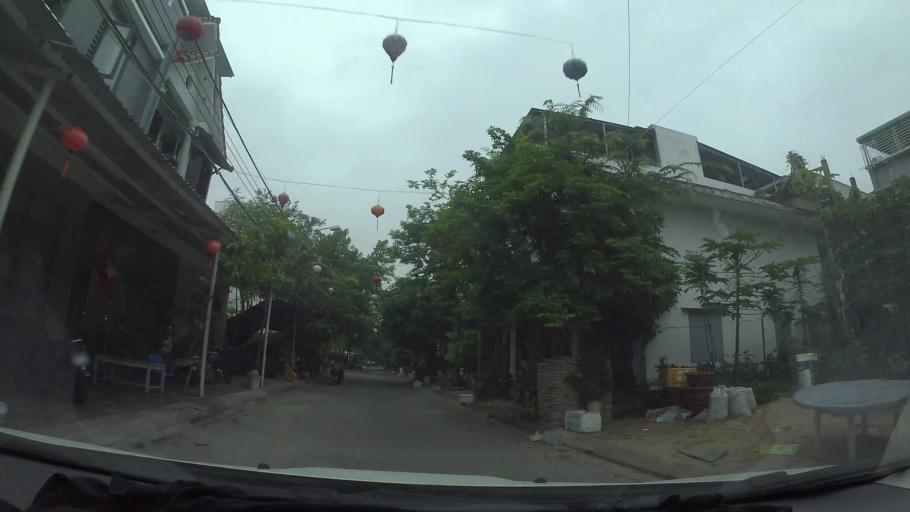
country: VN
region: Da Nang
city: Lien Chieu
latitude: 16.0792
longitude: 108.1592
